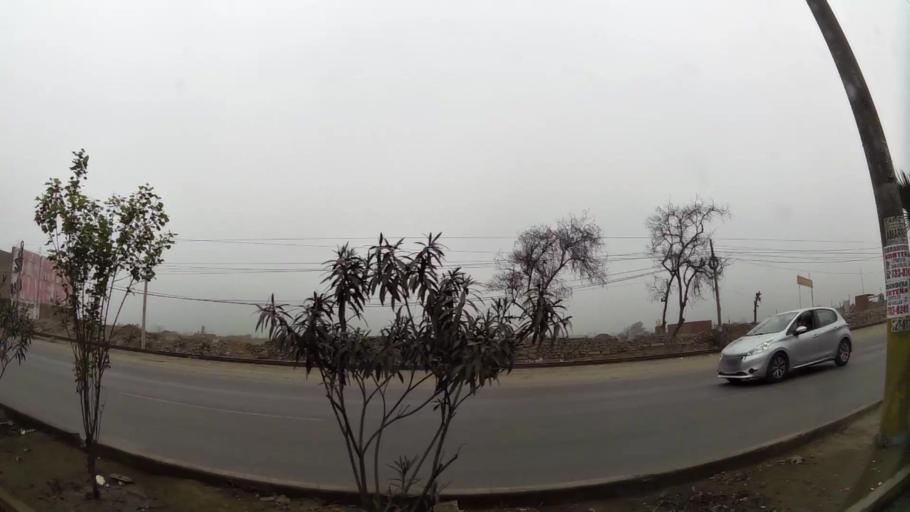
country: PE
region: Lima
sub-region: Lima
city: Santa Maria
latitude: -12.0070
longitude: -76.8534
